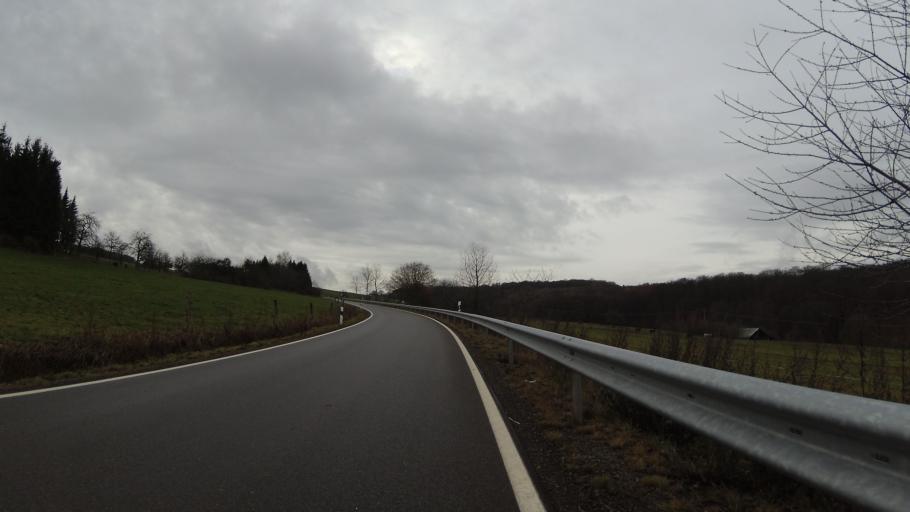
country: DE
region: Rheinland-Pfalz
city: Frohnhofen
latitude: 49.4495
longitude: 7.2972
